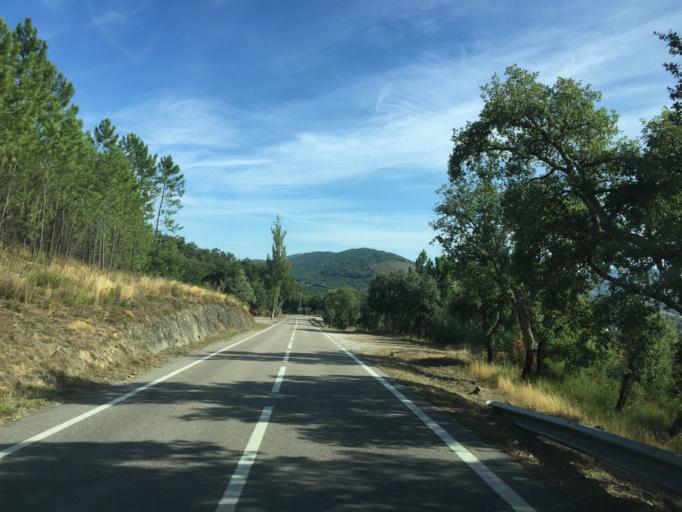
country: PT
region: Portalegre
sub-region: Marvao
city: Marvao
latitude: 39.3965
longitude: -7.3931
